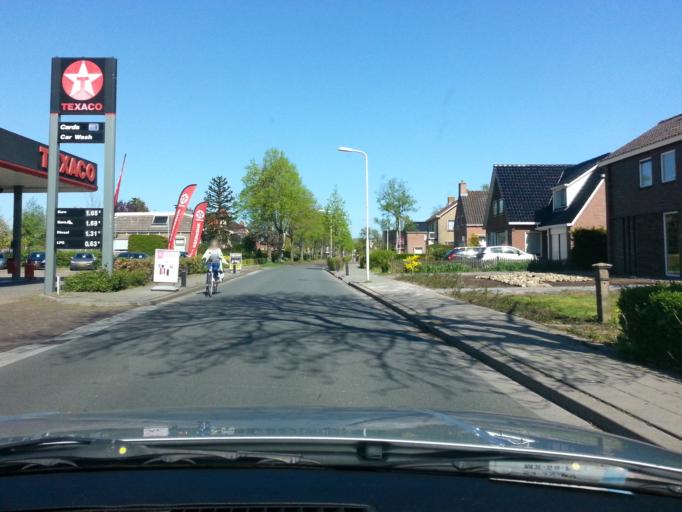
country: NL
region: Friesland
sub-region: Gemeente Achtkarspelen
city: Buitenpost
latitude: 53.2490
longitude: 6.1495
